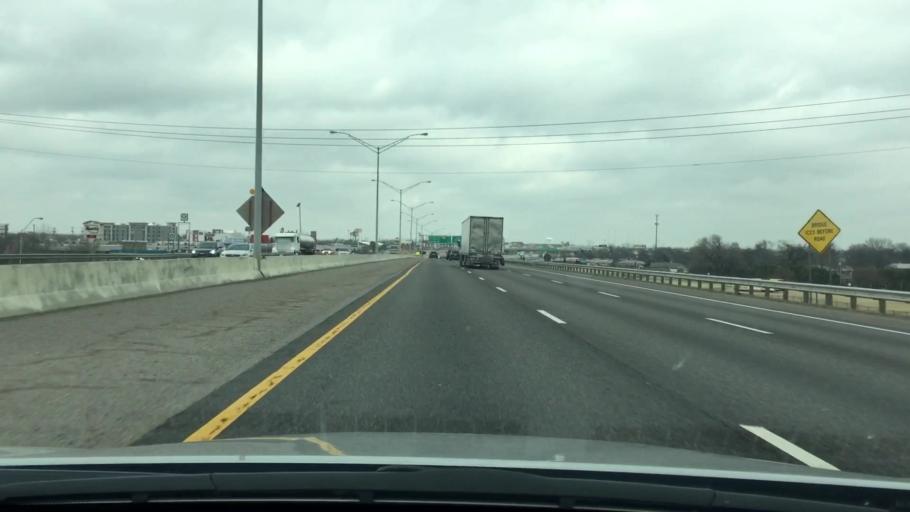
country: US
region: Oklahoma
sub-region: Cleveland County
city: Moore
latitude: 35.3412
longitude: -97.4928
